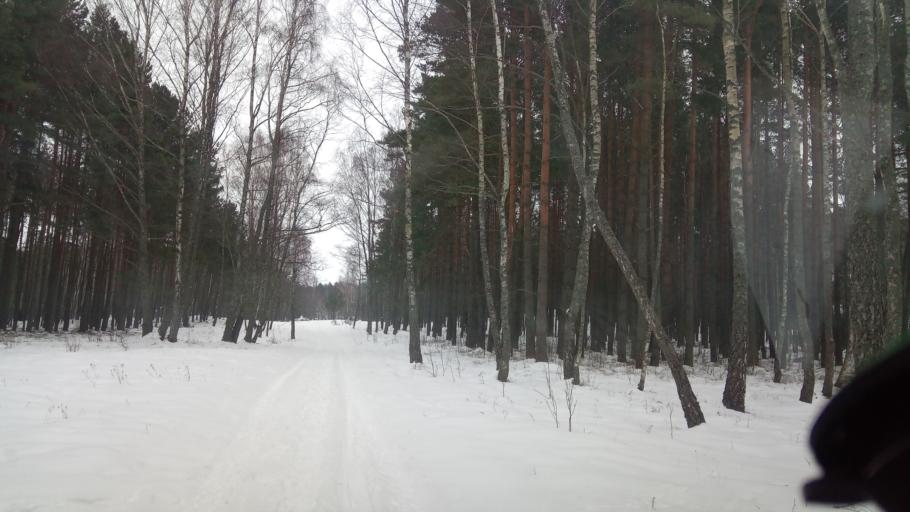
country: LT
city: Neringa
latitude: 55.4193
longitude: 21.1044
